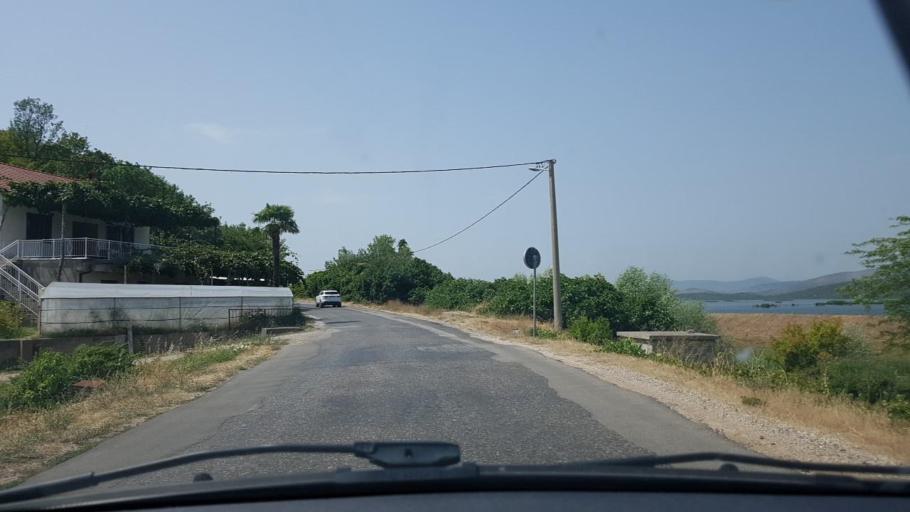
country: BA
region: Federation of Bosnia and Herzegovina
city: Tasovcici
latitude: 43.0184
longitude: 17.7732
